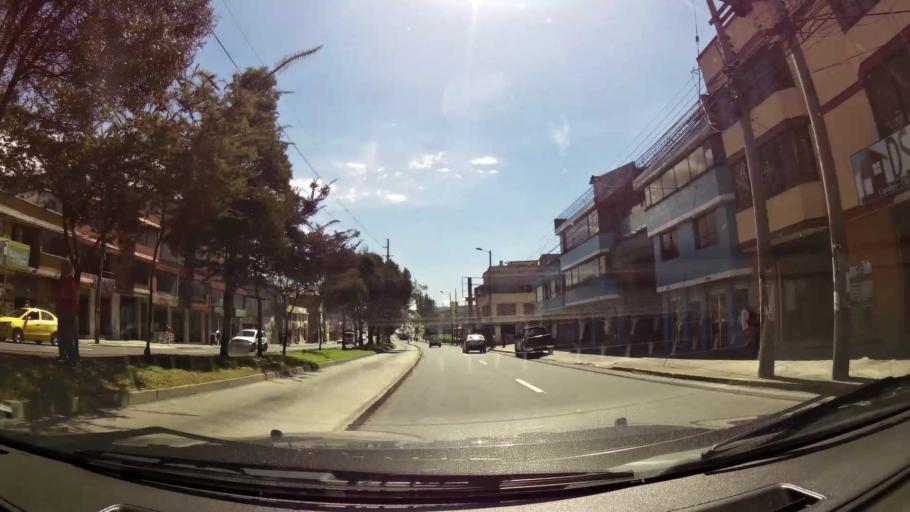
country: EC
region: Pichincha
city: Quito
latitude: -0.2549
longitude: -78.5409
